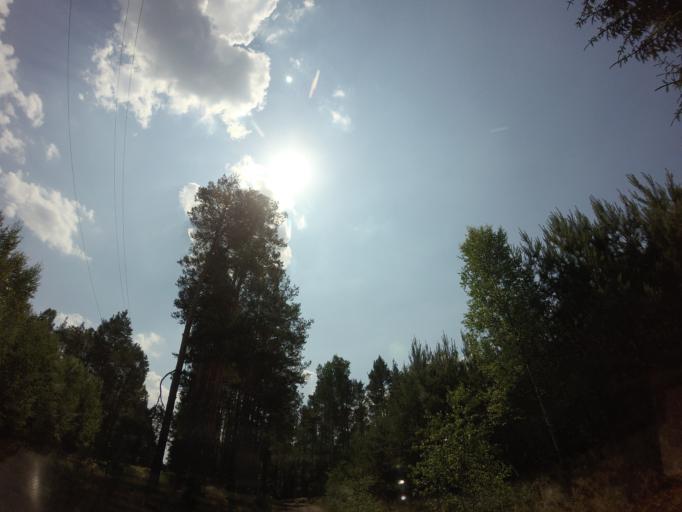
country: PL
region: West Pomeranian Voivodeship
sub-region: Powiat choszczenski
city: Bierzwnik
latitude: 53.0980
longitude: 15.7130
